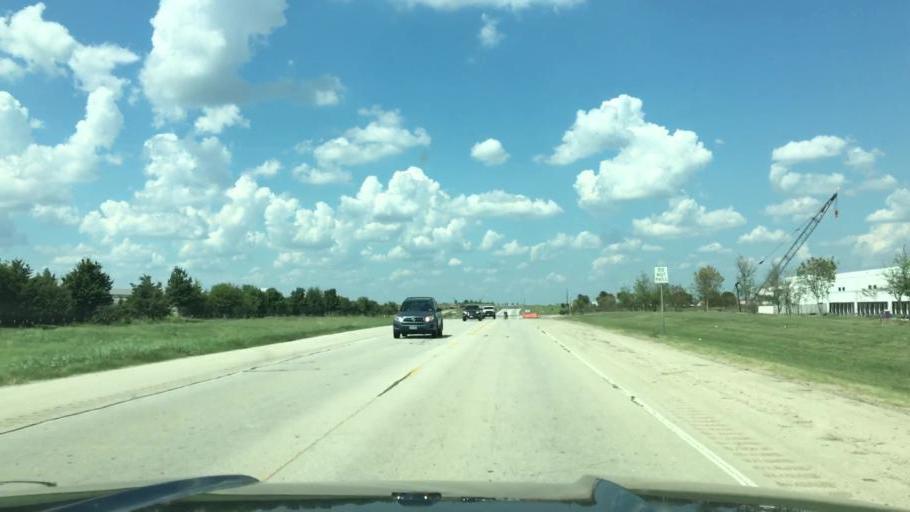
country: US
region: Texas
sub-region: Tarrant County
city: Haslet
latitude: 32.9857
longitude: -97.3420
